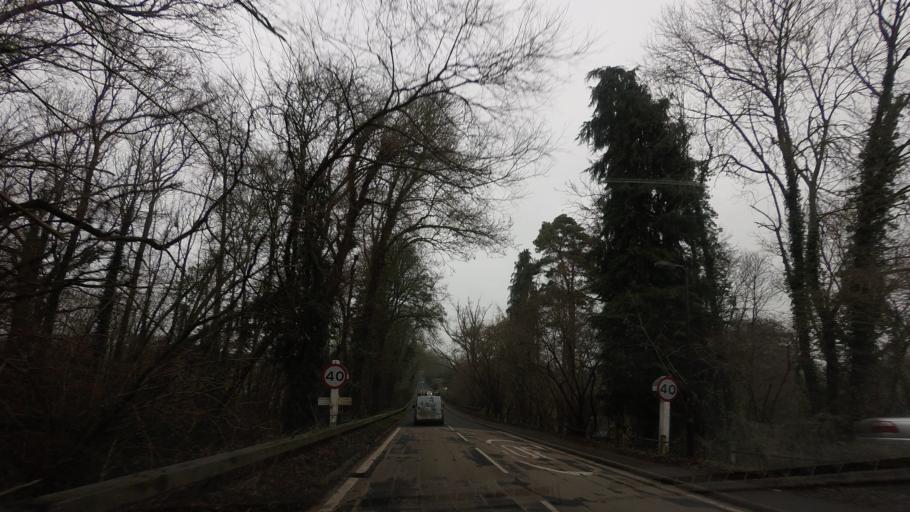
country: GB
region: England
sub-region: Kent
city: Hawkhurst
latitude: 51.0543
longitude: 0.5074
